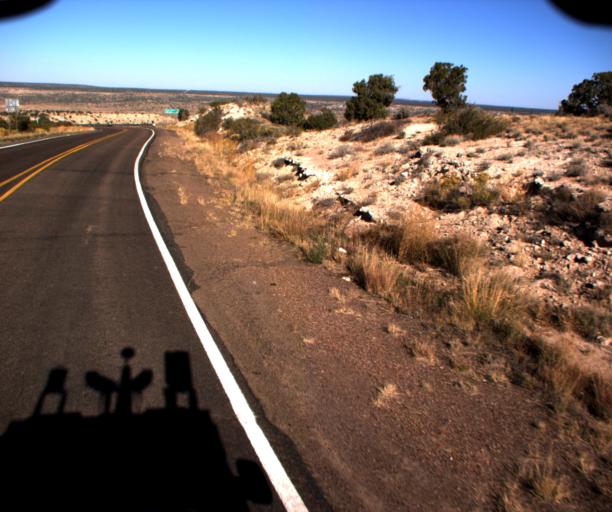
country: US
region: Arizona
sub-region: Navajo County
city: First Mesa
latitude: 35.7336
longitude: -110.1089
